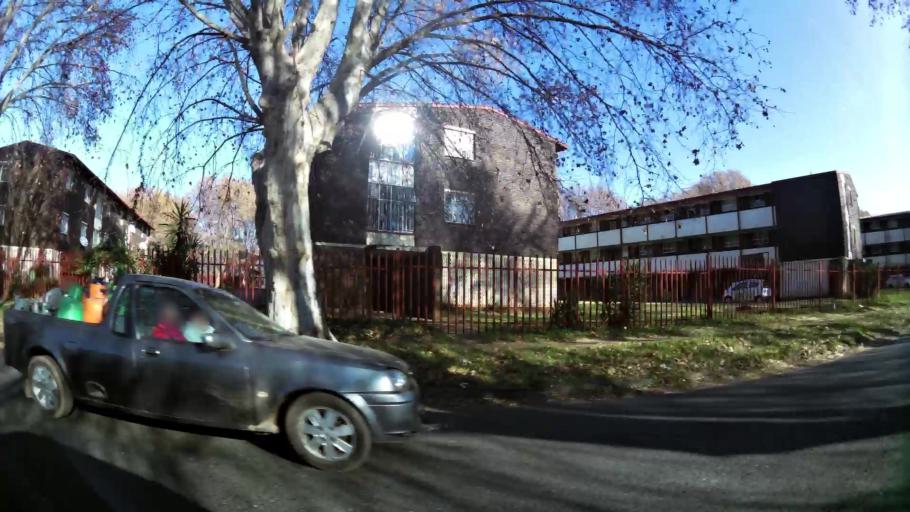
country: ZA
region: Gauteng
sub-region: City of Johannesburg Metropolitan Municipality
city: Johannesburg
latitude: -26.2061
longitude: 27.9896
